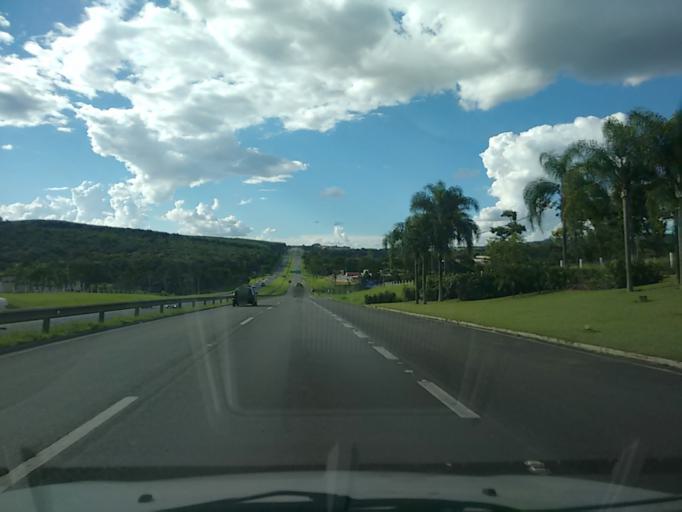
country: BR
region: Sao Paulo
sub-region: Sao Carlos
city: Sao Carlos
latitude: -22.0699
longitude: -47.8458
